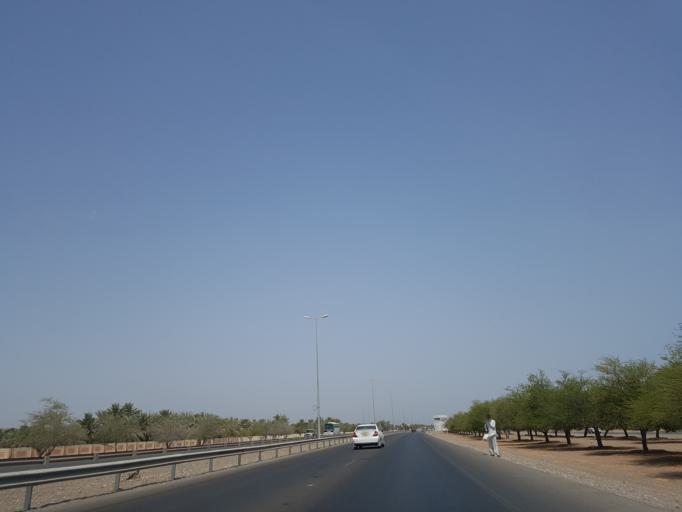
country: OM
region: Al Batinah
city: Saham
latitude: 24.0879
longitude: 56.9316
